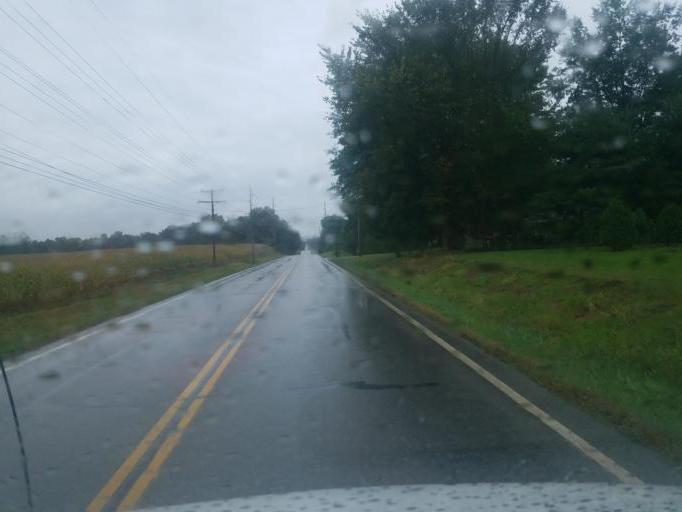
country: US
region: Ohio
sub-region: Medina County
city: Seville
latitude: 41.0252
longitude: -81.8391
